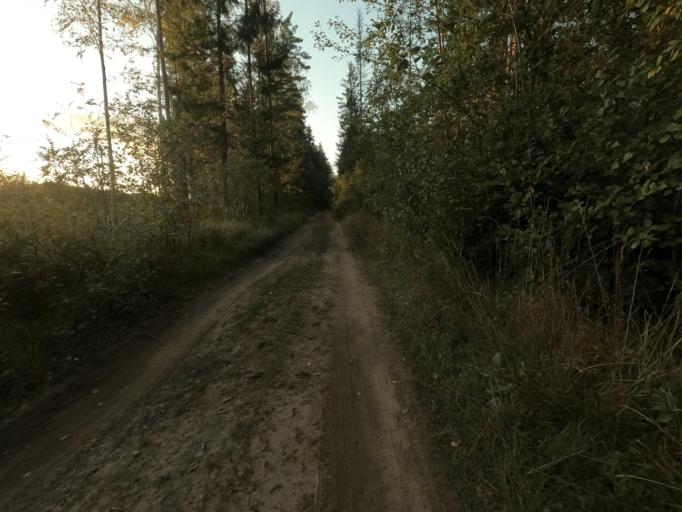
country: RU
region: Leningrad
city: Otradnoye
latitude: 59.8241
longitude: 30.8216
